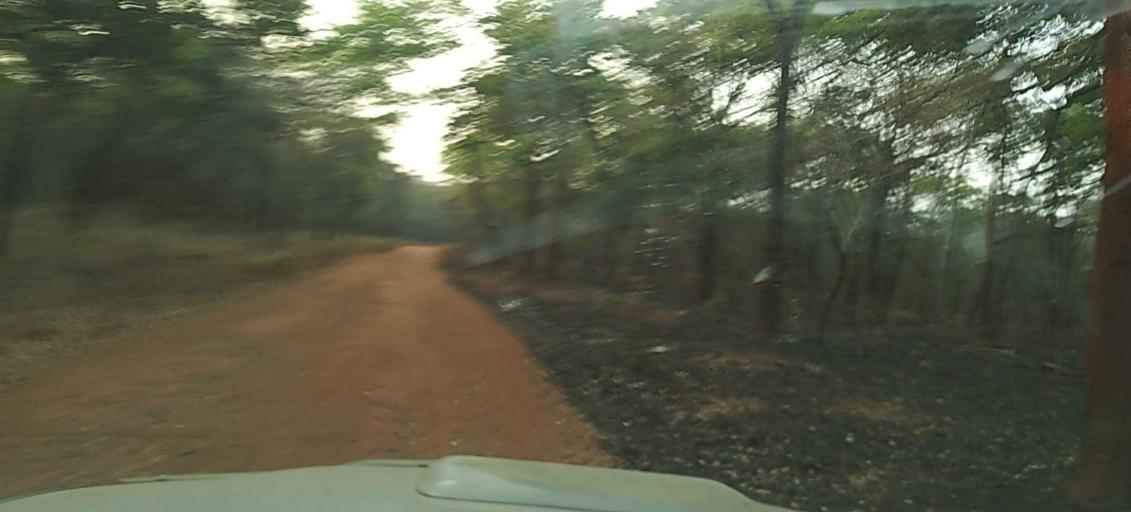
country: ZM
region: North-Western
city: Kasempa
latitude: -13.0973
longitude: 26.4023
